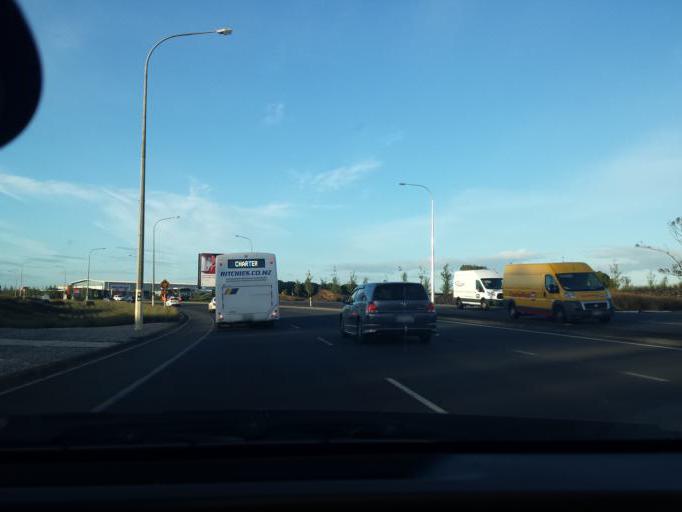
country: NZ
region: Auckland
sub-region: Auckland
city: Mangere
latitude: -36.9944
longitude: 174.7861
